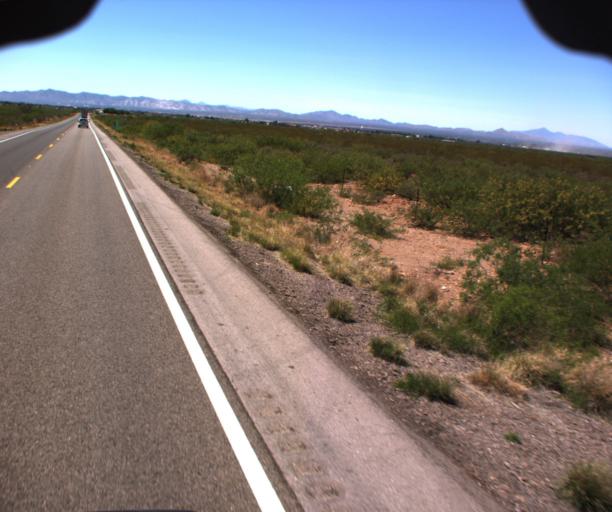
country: US
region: Arizona
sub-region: Cochise County
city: Douglas
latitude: 31.3901
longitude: -109.5120
